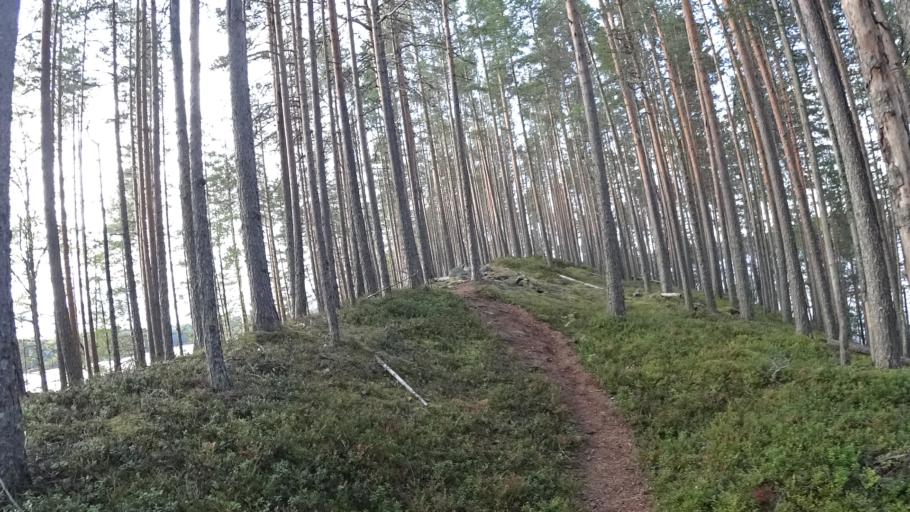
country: FI
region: North Karelia
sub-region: Joensuu
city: Ilomantsi
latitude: 62.5692
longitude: 31.1799
